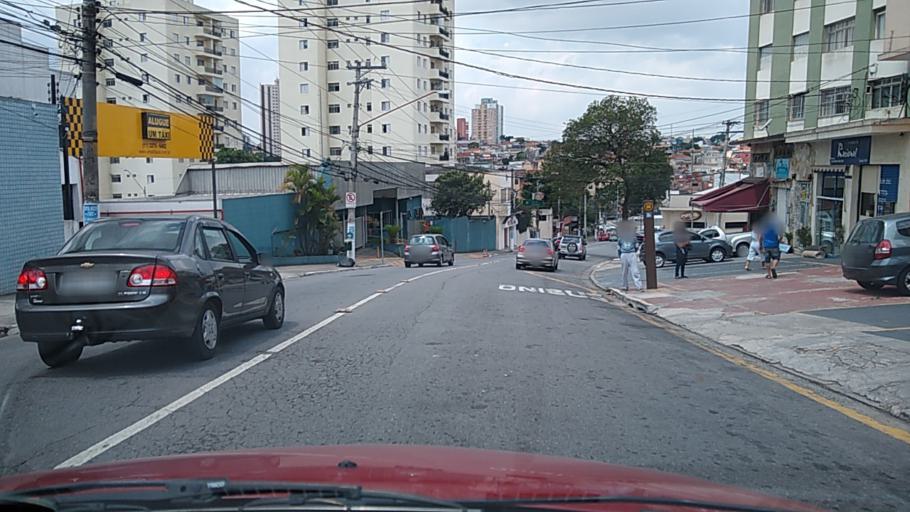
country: BR
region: Sao Paulo
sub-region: Diadema
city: Diadema
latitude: -23.6263
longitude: -46.6314
